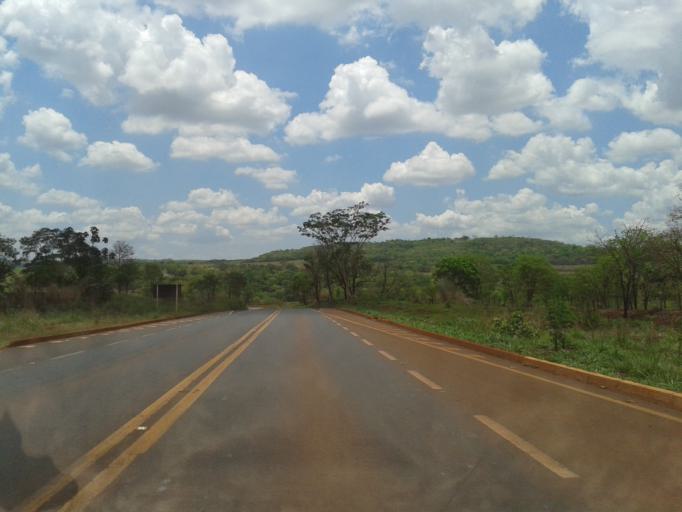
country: BR
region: Goias
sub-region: Itumbiara
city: Itumbiara
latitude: -18.3417
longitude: -49.4271
